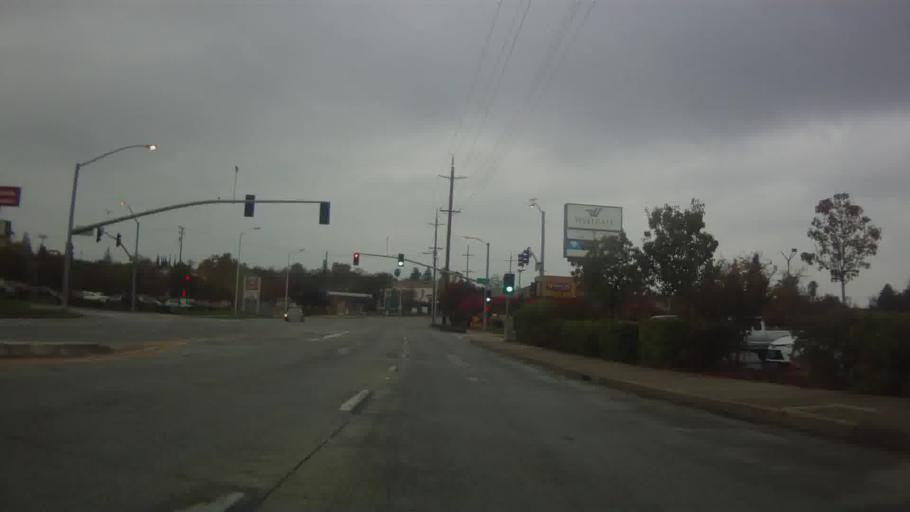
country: US
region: California
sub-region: Shasta County
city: Redding
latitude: 40.5867
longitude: -122.3967
